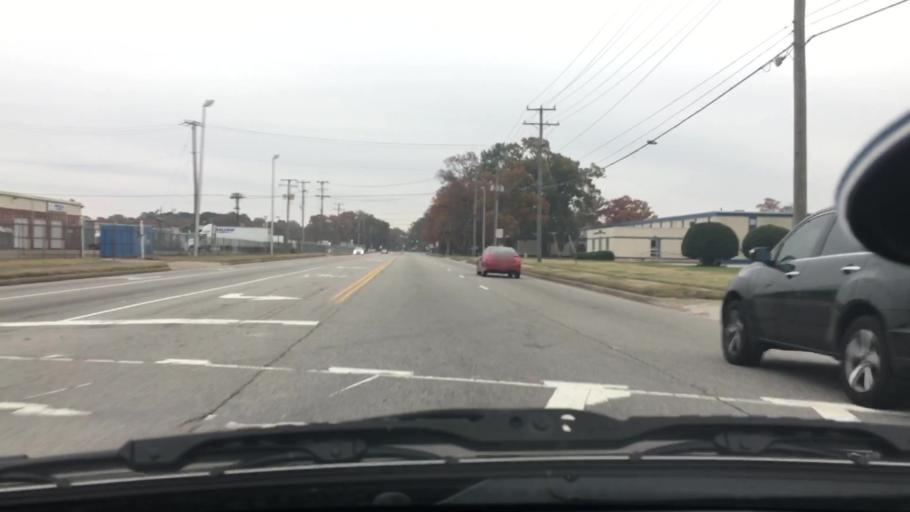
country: US
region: Virginia
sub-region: City of Norfolk
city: Norfolk
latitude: 36.8586
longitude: -76.2422
